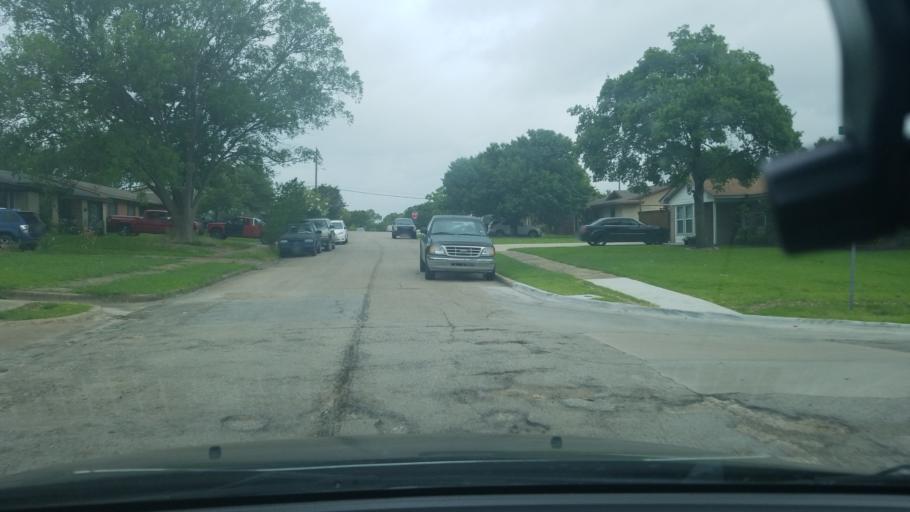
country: US
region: Texas
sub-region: Dallas County
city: Mesquite
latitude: 32.7844
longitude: -96.6359
